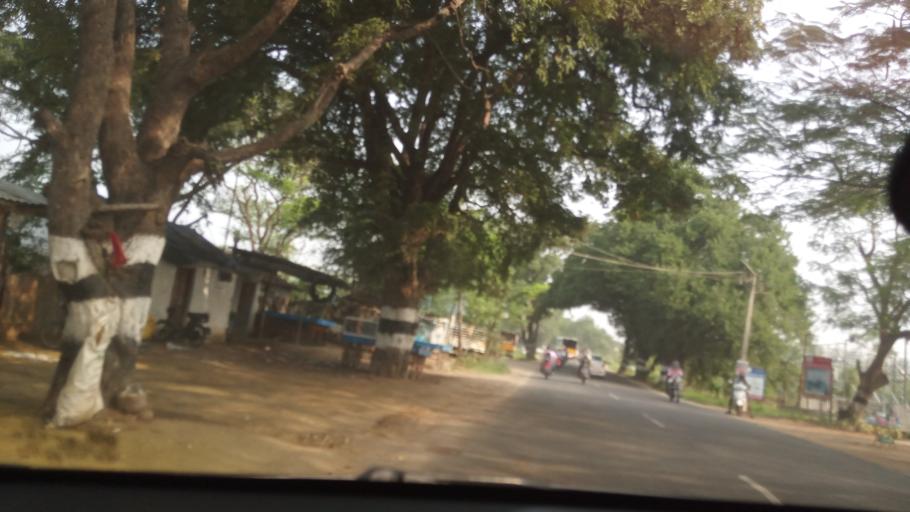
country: IN
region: Tamil Nadu
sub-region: Coimbatore
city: Periyanayakkanpalaiyam
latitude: 11.1533
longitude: 77.0496
